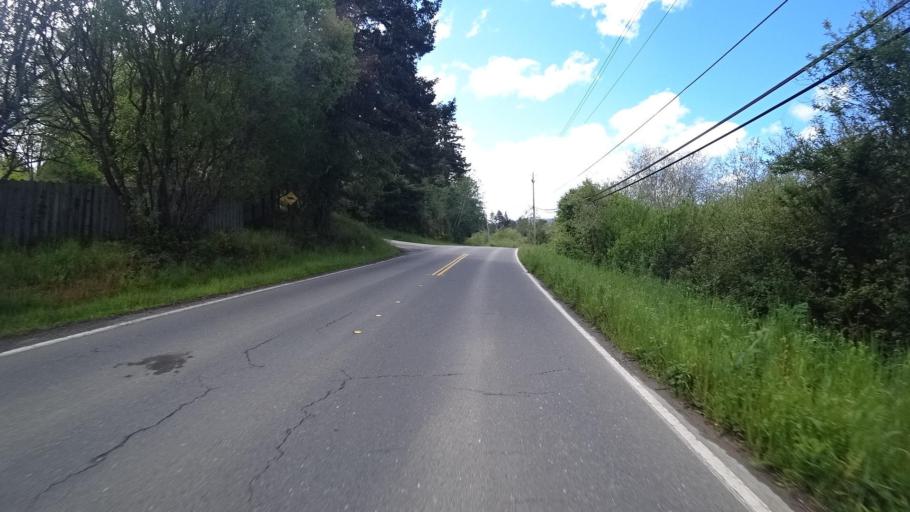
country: US
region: California
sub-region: Humboldt County
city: Blue Lake
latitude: 40.9066
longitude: -124.0253
